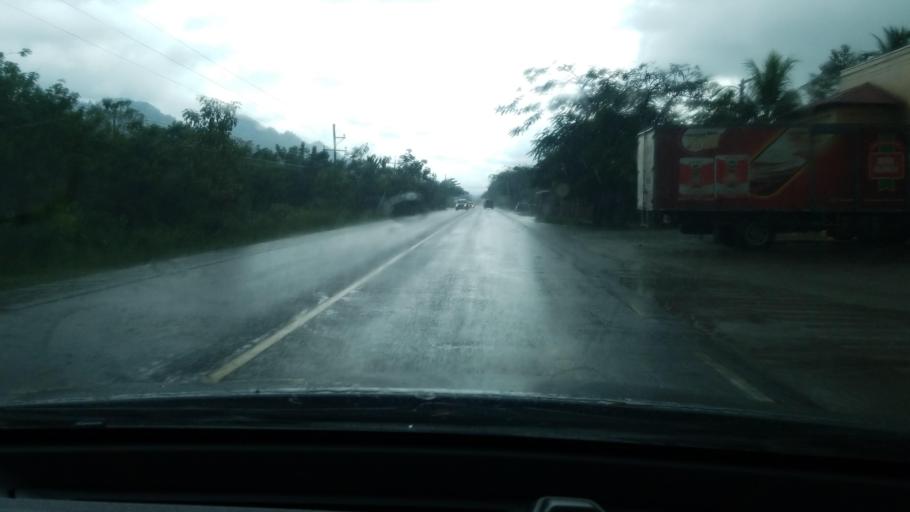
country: HN
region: Cortes
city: Rio Chiquito
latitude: 15.6279
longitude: -88.2542
